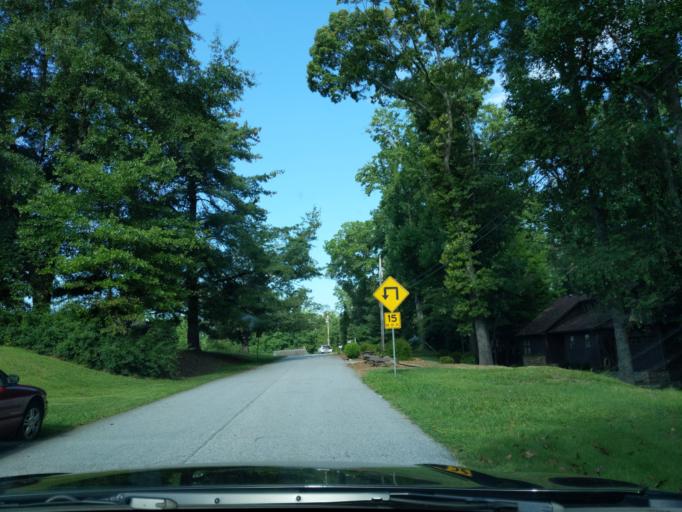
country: US
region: South Carolina
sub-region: Greenville County
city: Mauldin
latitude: 34.8004
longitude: -82.3212
